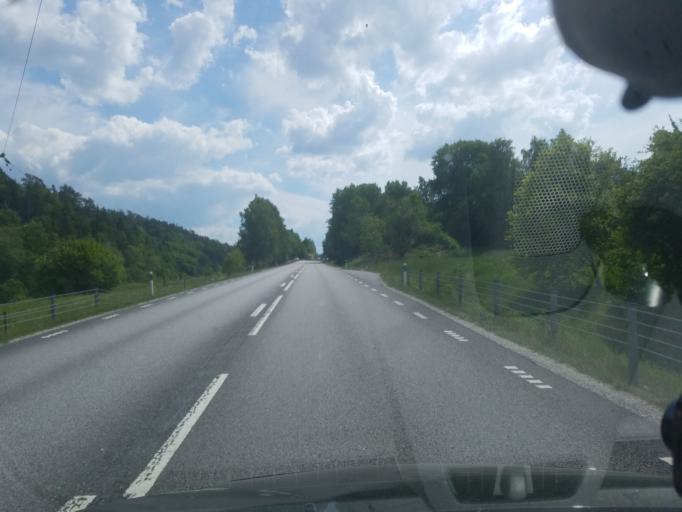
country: SE
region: Vaestra Goetaland
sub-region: Orust
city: Henan
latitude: 58.2184
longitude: 11.6894
